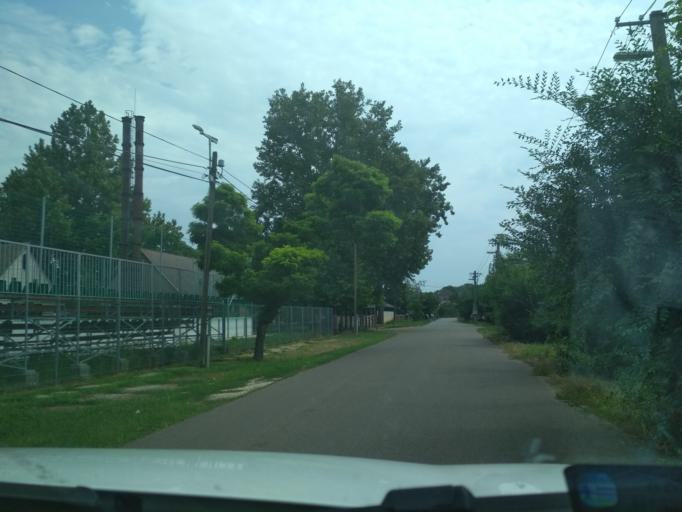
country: HU
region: Jasz-Nagykun-Szolnok
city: Tiszafured
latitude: 47.6204
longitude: 20.7502
